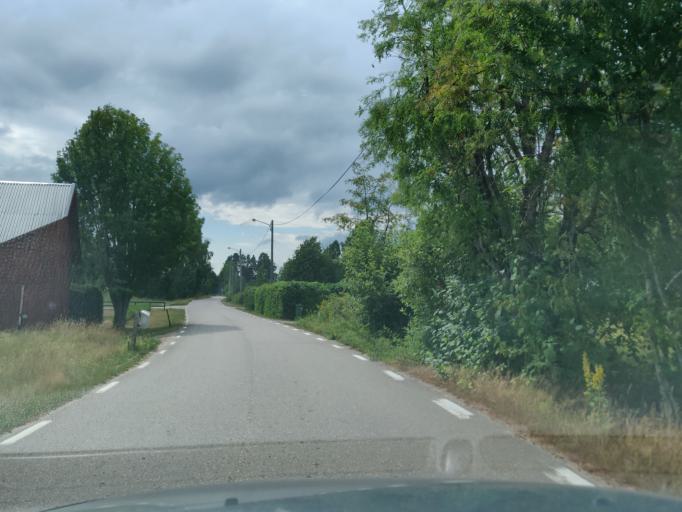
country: SE
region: Vaermland
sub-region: Munkfors Kommun
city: Munkfors
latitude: 59.8833
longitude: 13.5605
